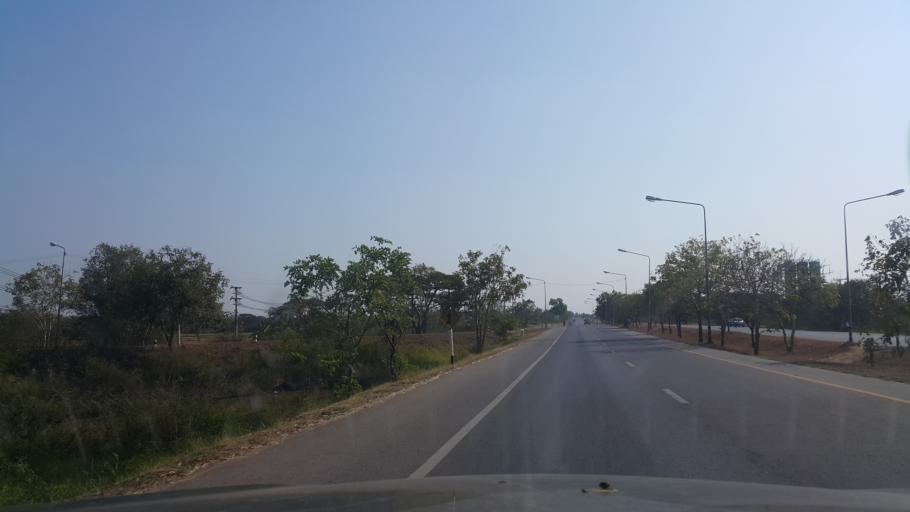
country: TH
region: Khon Kaen
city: Khon Kaen
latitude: 16.4352
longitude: 102.9179
